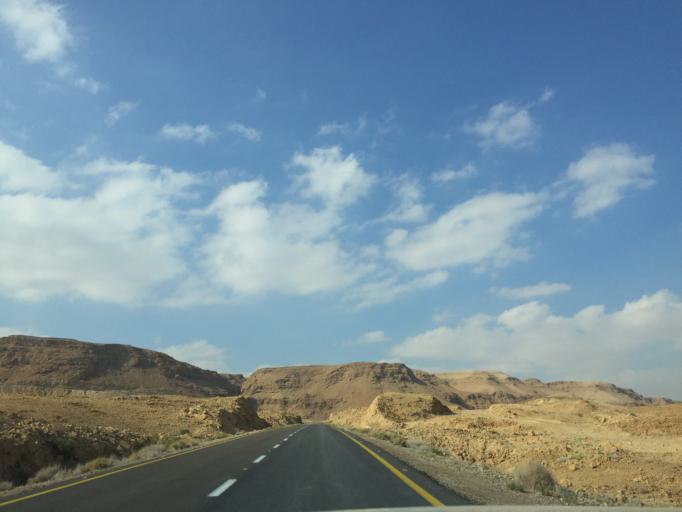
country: IL
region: Southern District
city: `En Boqeq
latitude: 31.3198
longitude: 35.3411
